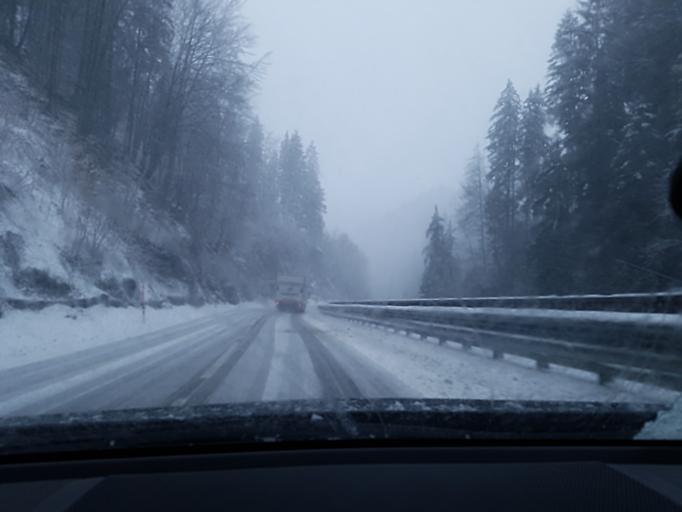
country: AT
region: Salzburg
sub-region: Politischer Bezirk Hallein
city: Abtenau
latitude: 47.5944
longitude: 13.3048
